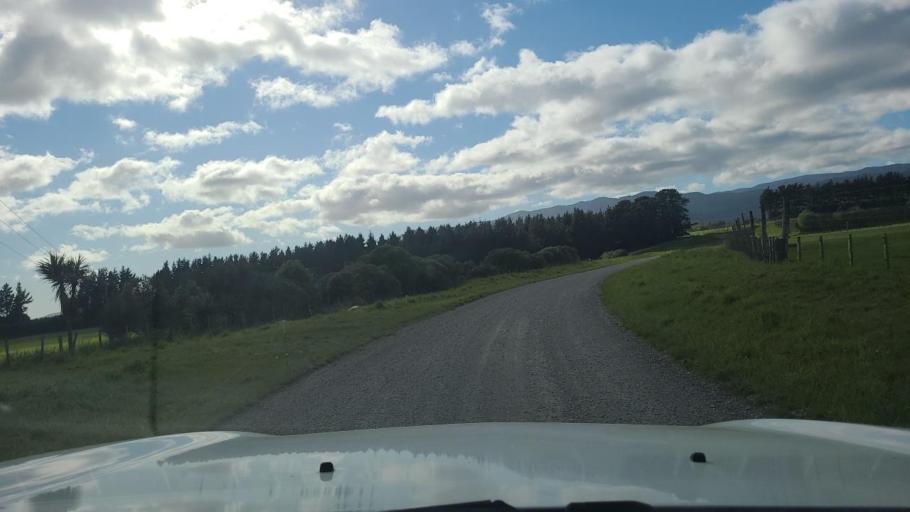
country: NZ
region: Wellington
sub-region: Upper Hutt City
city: Upper Hutt
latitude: -41.3432
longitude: 175.2133
